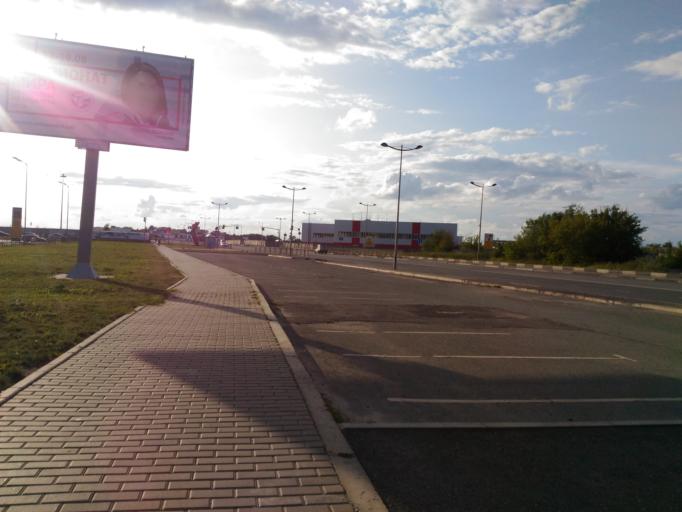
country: RU
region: Ulyanovsk
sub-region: Ulyanovskiy Rayon
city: Ulyanovsk
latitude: 54.2871
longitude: 48.2791
